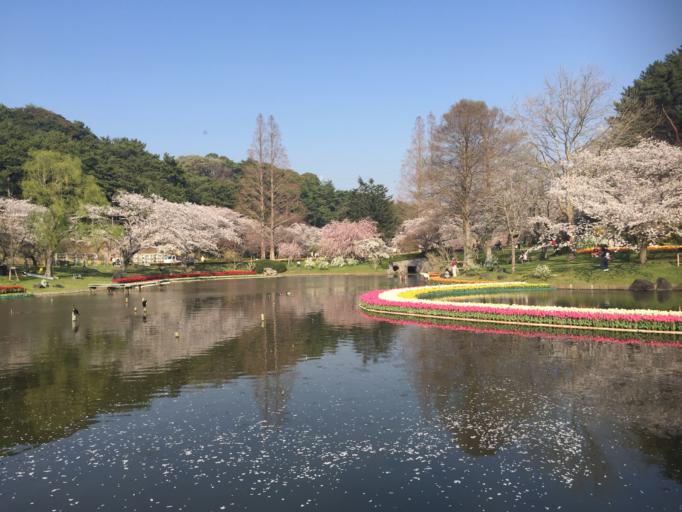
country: JP
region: Shizuoka
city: Kosai-shi
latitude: 34.7640
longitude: 137.6304
